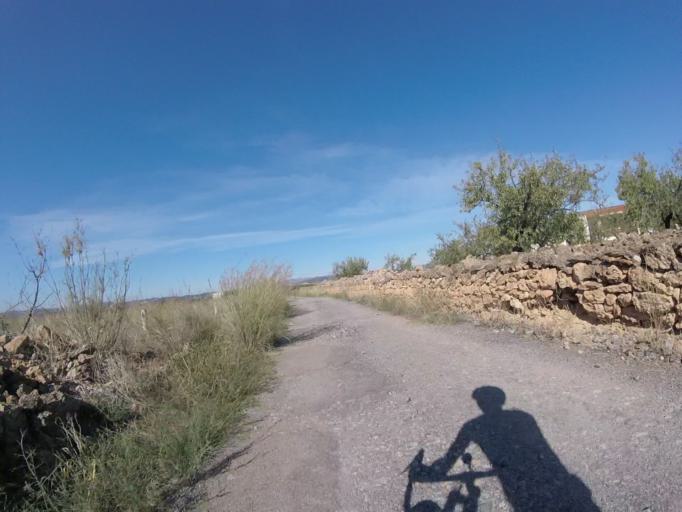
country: ES
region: Valencia
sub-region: Provincia de Castello
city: Torreblanca
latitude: 40.2101
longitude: 0.2320
